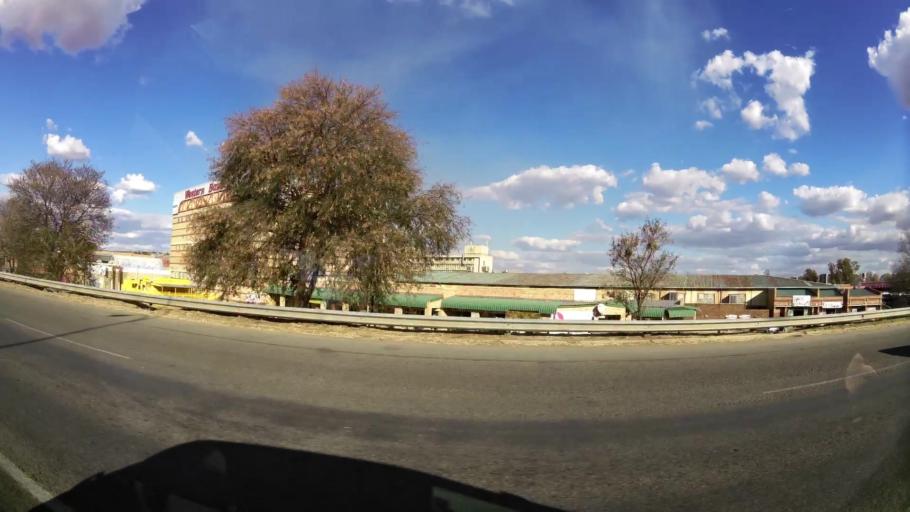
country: ZA
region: North-West
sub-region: Dr Kenneth Kaunda District Municipality
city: Klerksdorp
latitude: -26.8622
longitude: 26.6619
